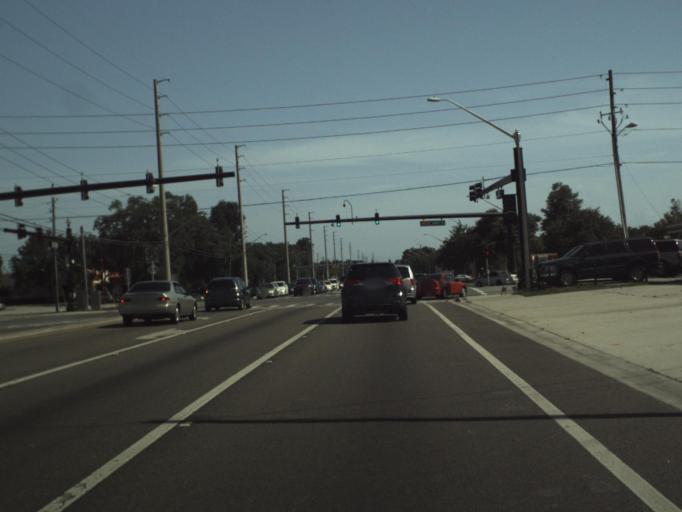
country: US
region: Florida
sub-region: Seminole County
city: Oviedo
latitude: 28.6564
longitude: -81.2083
